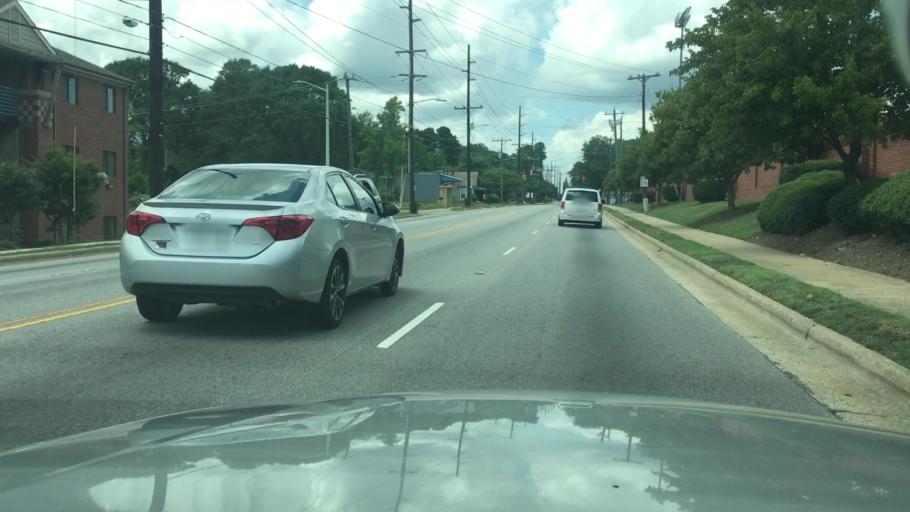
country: US
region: North Carolina
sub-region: Cumberland County
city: Fayetteville
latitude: 35.0746
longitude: -78.8967
